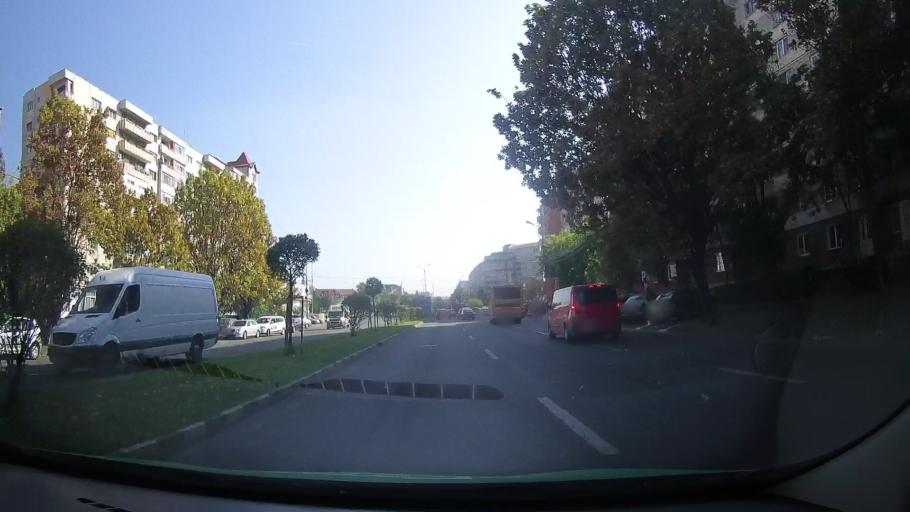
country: RO
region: Bihor
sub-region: Comuna Biharea
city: Oradea
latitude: 47.0700
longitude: 21.9227
